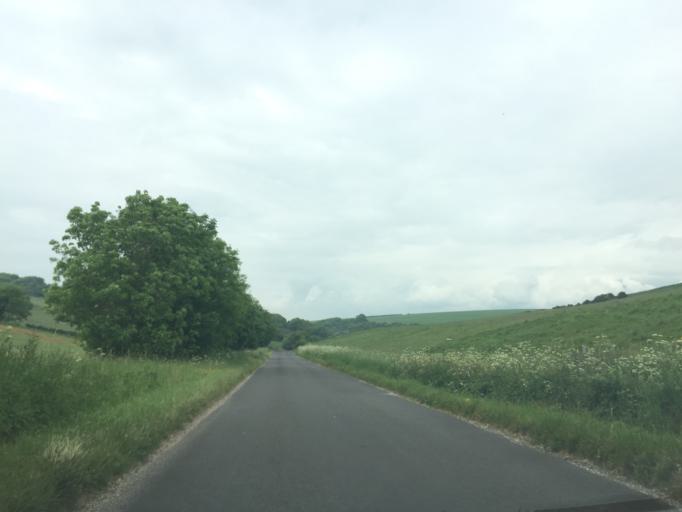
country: GB
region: England
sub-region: Dorset
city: Wool
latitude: 50.6400
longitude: -2.2670
